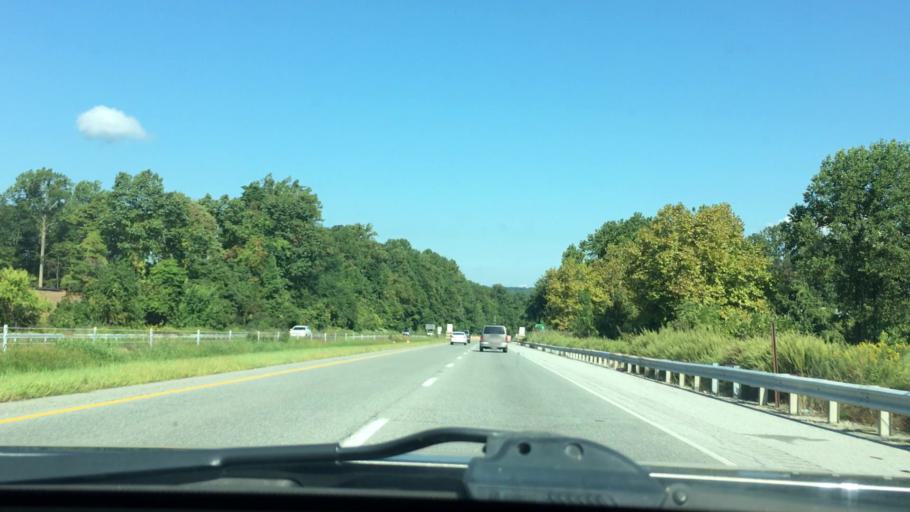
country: US
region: Pennsylvania
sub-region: Chester County
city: Exton
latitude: 40.0219
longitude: -75.5873
